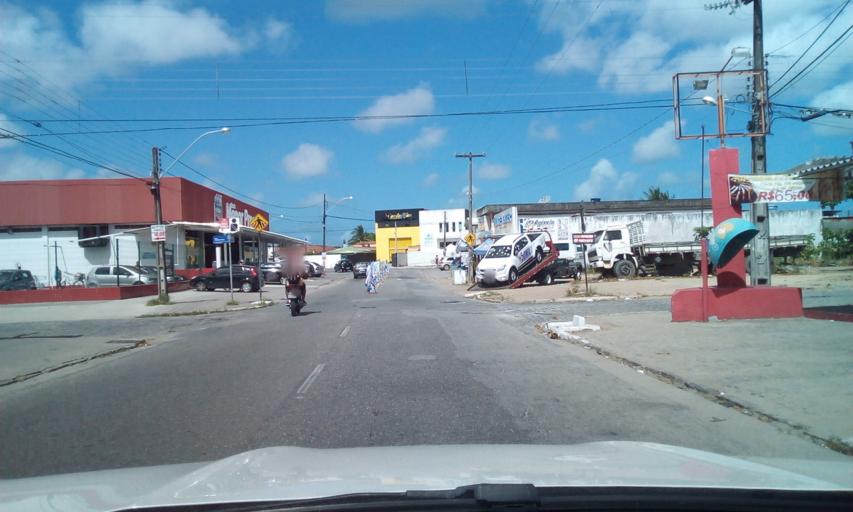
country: BR
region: Paraiba
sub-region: Joao Pessoa
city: Joao Pessoa
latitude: -7.1555
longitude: -34.8726
